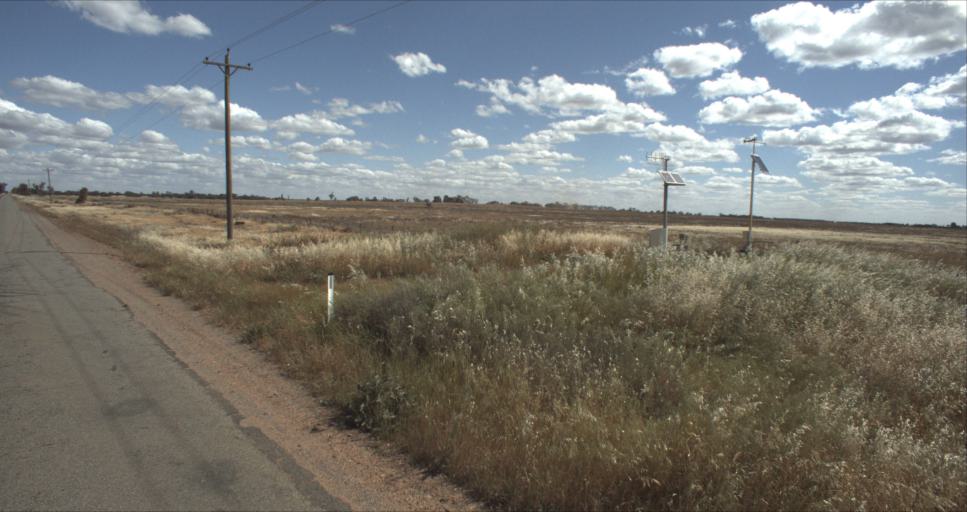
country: AU
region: New South Wales
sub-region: Leeton
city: Leeton
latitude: -34.4748
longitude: 146.2502
